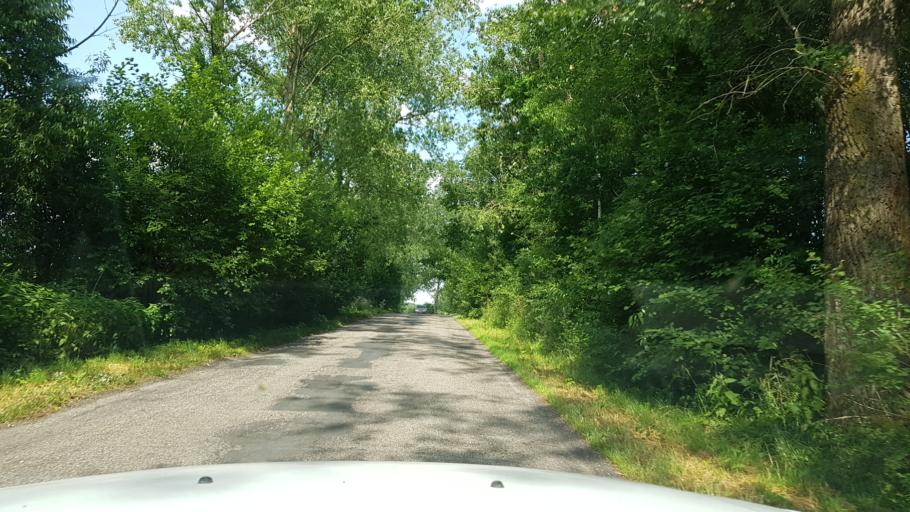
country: PL
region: West Pomeranian Voivodeship
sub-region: Powiat goleniowski
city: Osina
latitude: 53.5942
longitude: 14.9945
